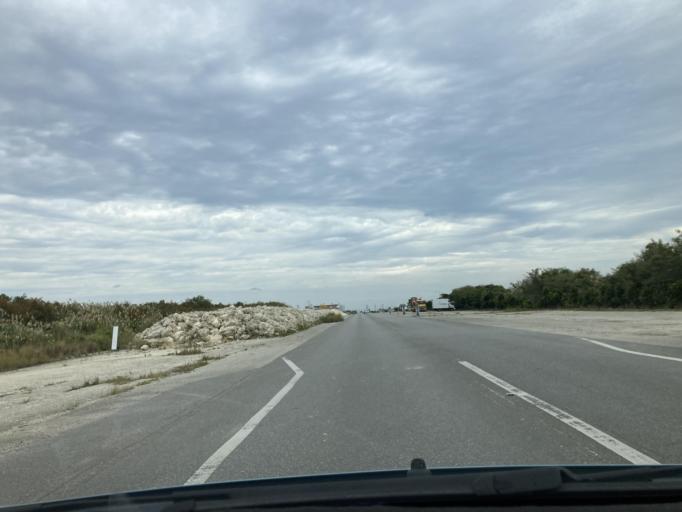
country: JP
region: Okinawa
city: Okinawa
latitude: 26.3877
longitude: 127.7462
